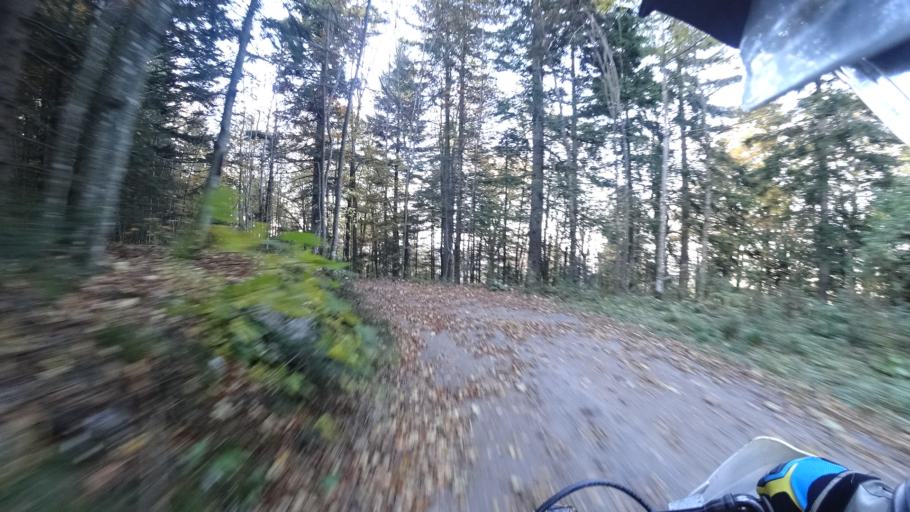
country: HR
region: Karlovacka
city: Plaski
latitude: 44.9626
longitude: 15.4367
